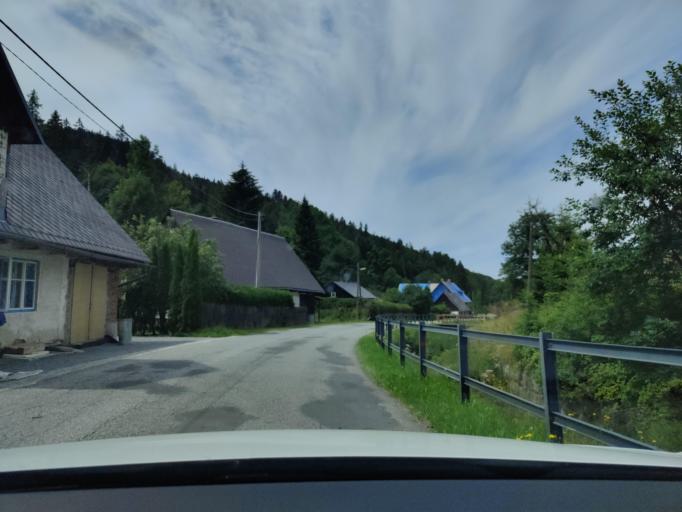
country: CZ
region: Olomoucky
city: Zlate Hory
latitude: 50.2206
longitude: 17.3469
